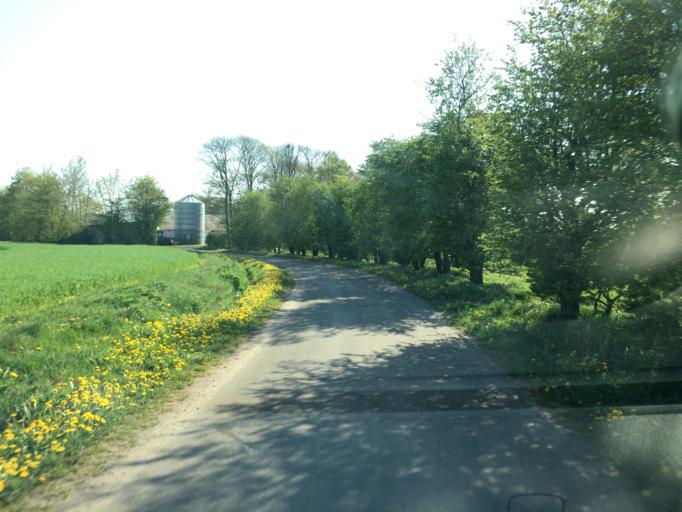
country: DK
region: South Denmark
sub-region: Tonder Kommune
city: Toftlund
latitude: 55.1687
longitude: 9.1006
